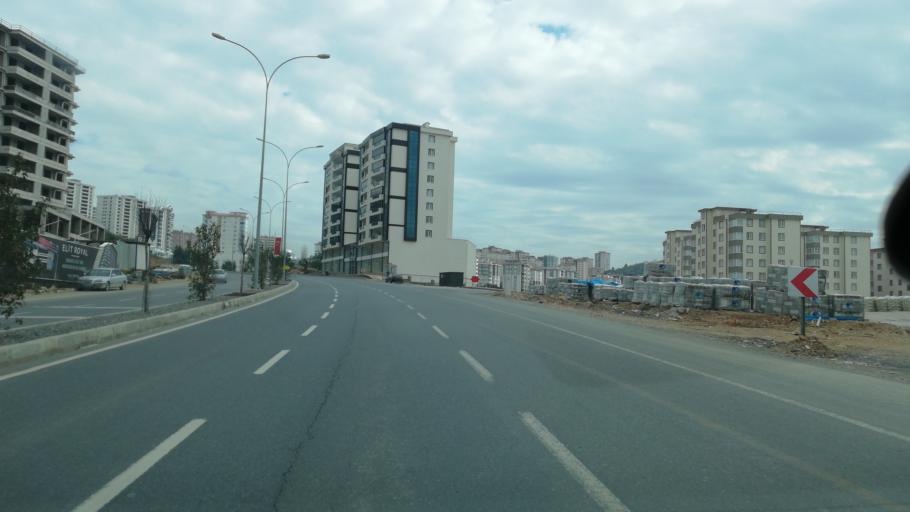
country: TR
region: Kahramanmaras
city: Kahramanmaras
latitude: 37.5850
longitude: 36.8514
